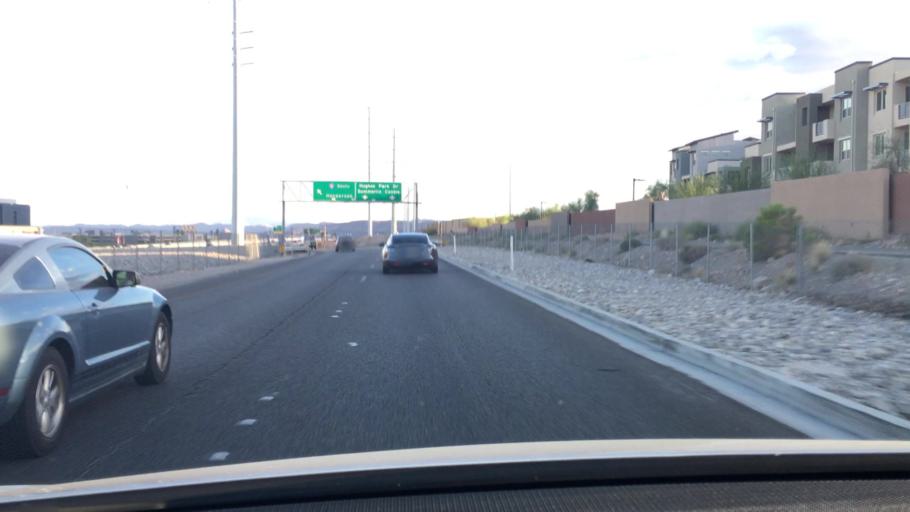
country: US
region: Nevada
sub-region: Clark County
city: Summerlin South
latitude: 36.1583
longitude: -115.3384
